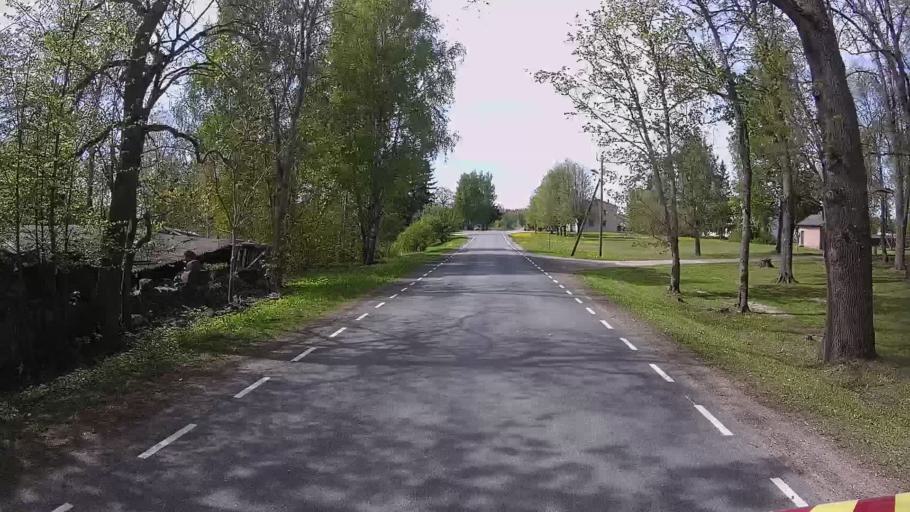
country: EE
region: Valgamaa
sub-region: Valga linn
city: Valga
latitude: 57.6938
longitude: 26.2713
